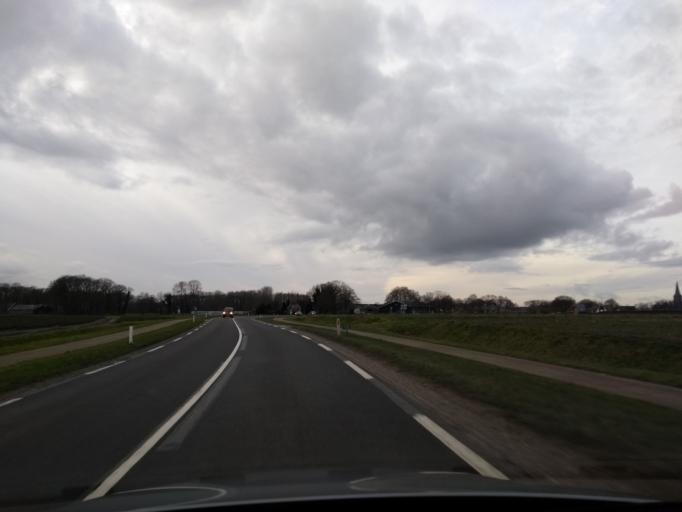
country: NL
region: Overijssel
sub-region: Gemeente Hengelo
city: Hengelo
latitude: 52.2945
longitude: 6.8435
